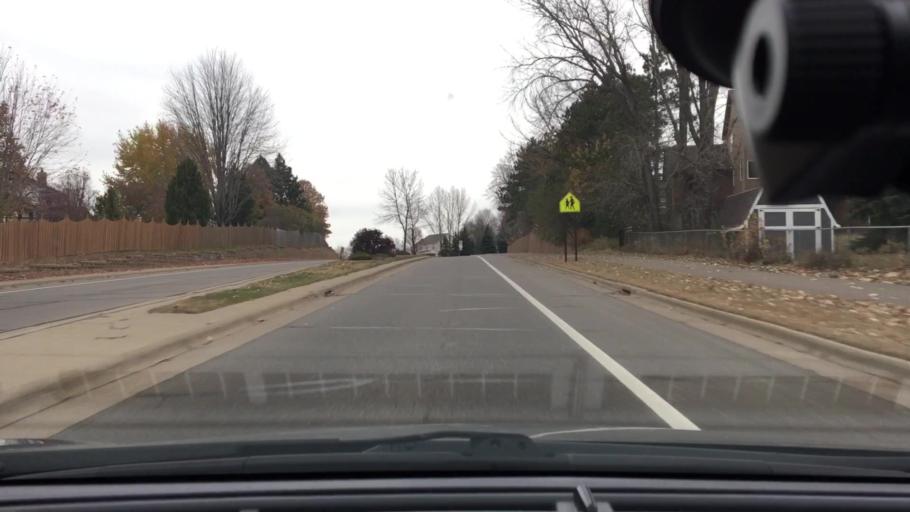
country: US
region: Minnesota
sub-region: Hennepin County
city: Corcoran
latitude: 45.1125
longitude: -93.5119
